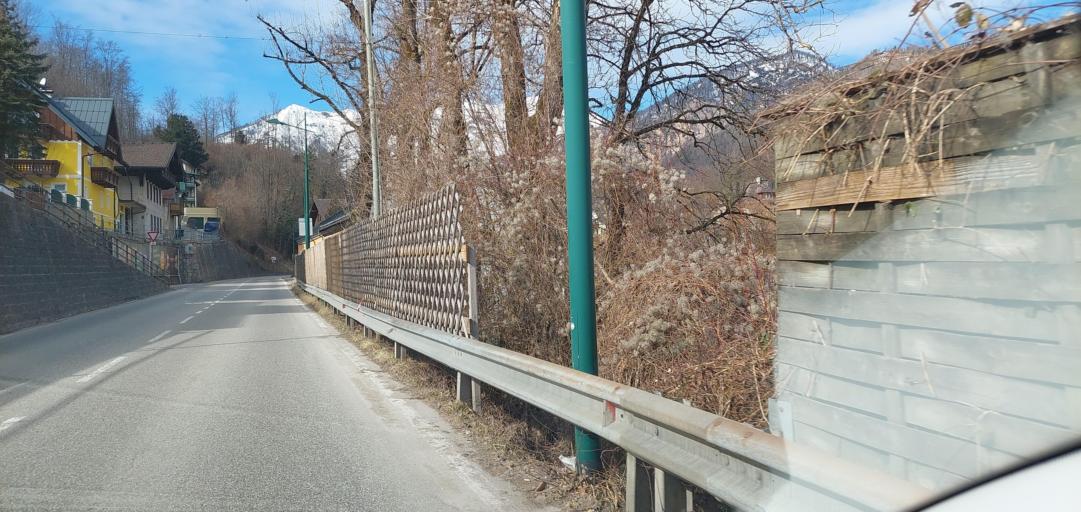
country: AT
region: Upper Austria
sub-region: Politischer Bezirk Gmunden
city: Bad Ischl
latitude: 47.7143
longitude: 13.6163
